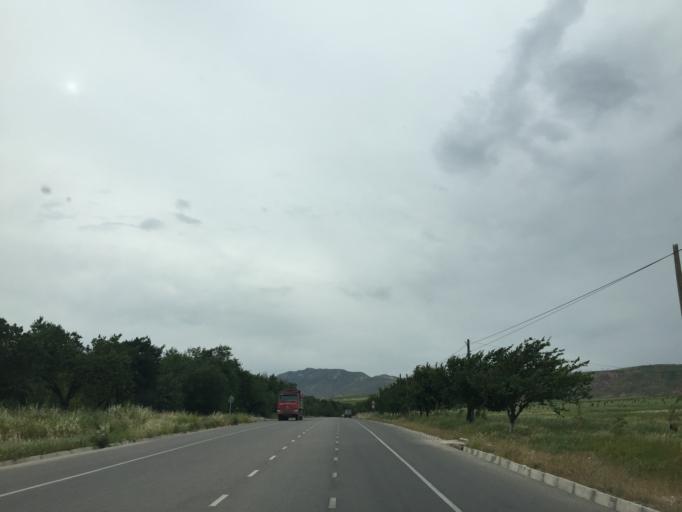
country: TJ
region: Republican Subordination
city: Vahdat
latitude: 38.5082
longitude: 69.1177
